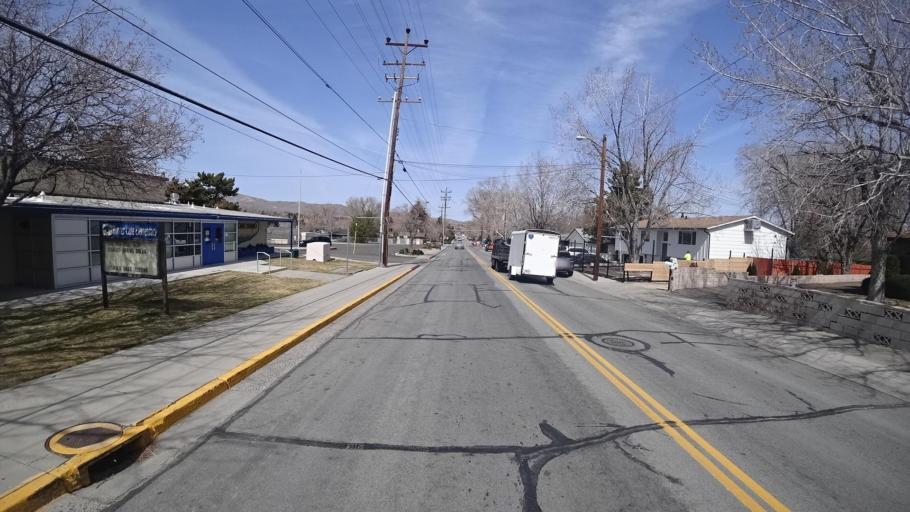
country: US
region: Nevada
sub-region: Washoe County
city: Reno
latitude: 39.5112
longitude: -119.8359
